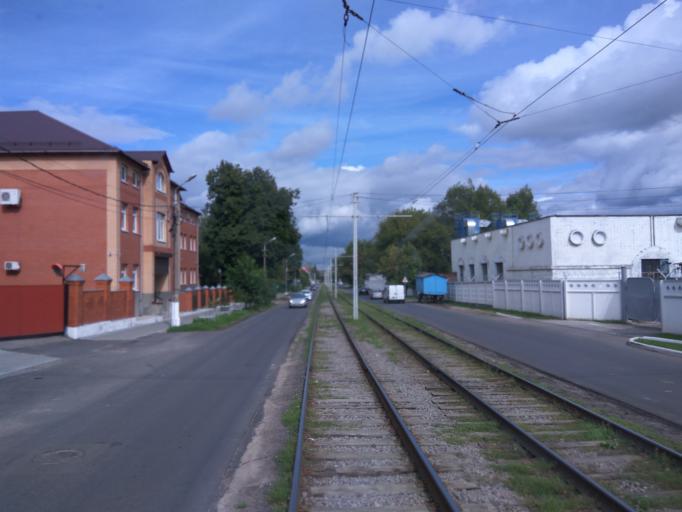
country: RU
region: Moskovskaya
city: Kolomna
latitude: 55.0961
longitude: 38.7713
